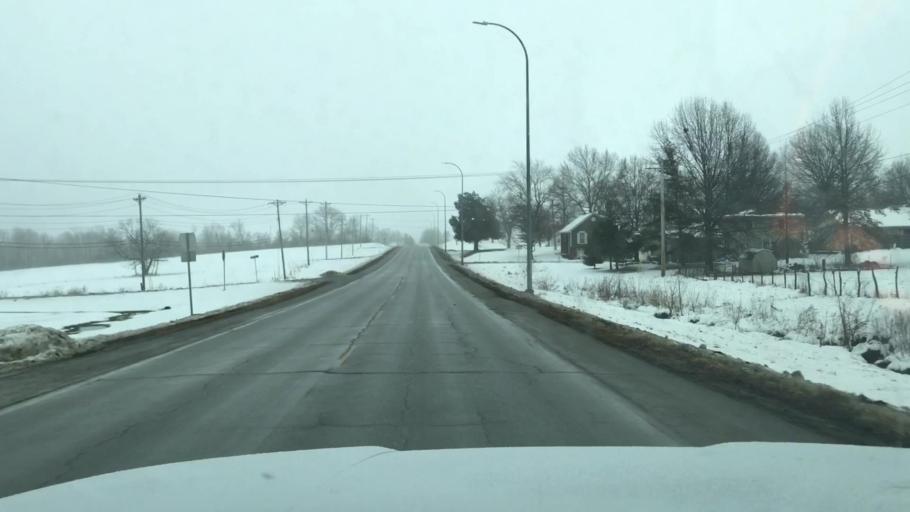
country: US
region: Missouri
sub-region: Clinton County
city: Cameron
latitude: 39.7318
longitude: -94.2335
